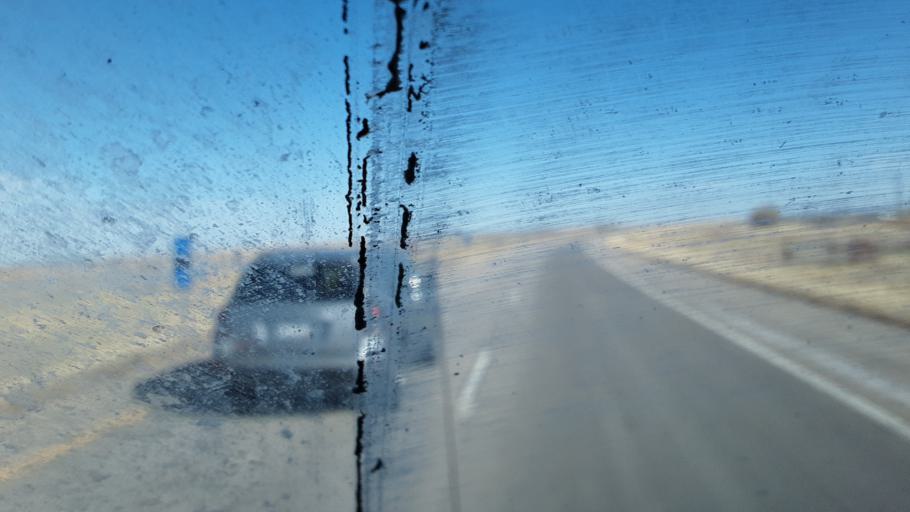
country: US
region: Colorado
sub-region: Weld County
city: Keenesburg
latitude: 40.1100
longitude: -104.5740
